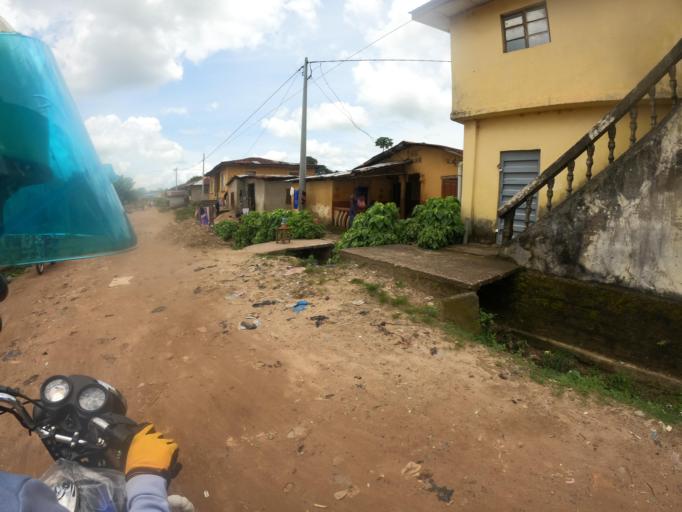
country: SL
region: Northern Province
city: Makeni
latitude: 8.8905
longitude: -12.0500
